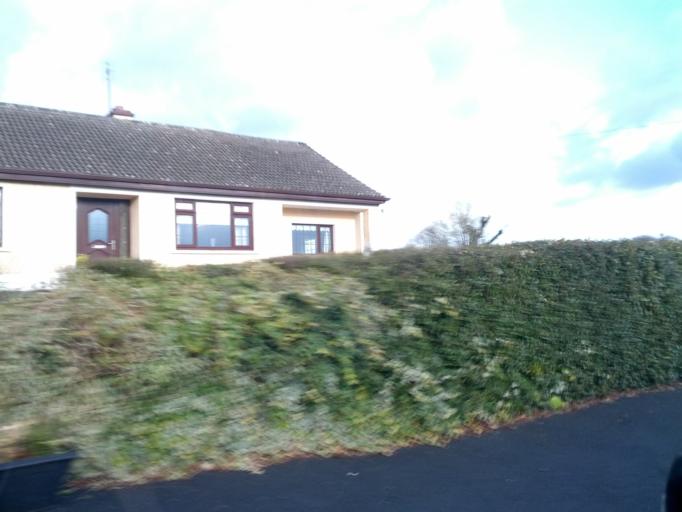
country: IE
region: Connaught
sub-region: County Galway
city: Athenry
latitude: 53.3679
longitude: -8.6509
